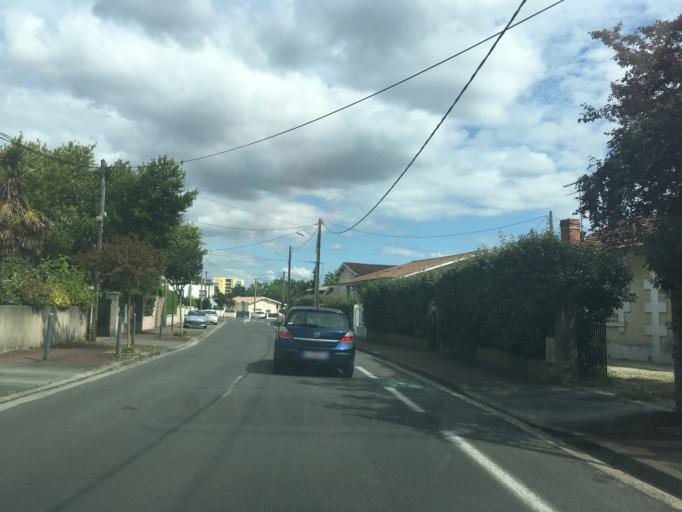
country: FR
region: Aquitaine
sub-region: Departement de la Gironde
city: Merignac
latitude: 44.8480
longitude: -0.6404
